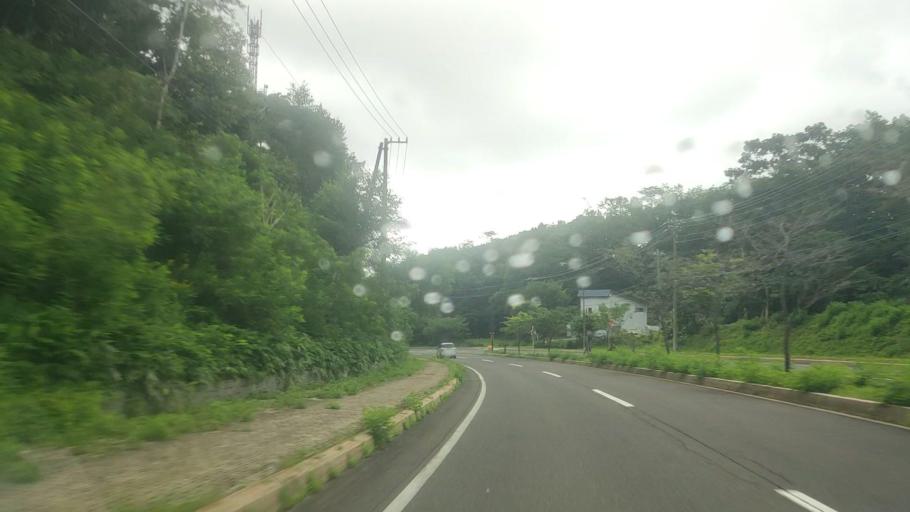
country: JP
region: Hokkaido
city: Shiraoi
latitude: 42.4706
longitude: 141.1487
